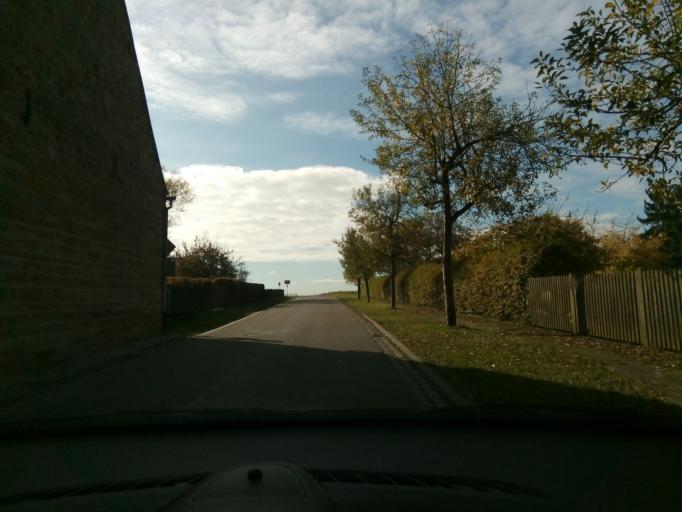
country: DE
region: Bavaria
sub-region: Regierungsbezirk Unterfranken
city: Oberschwarzach
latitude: 49.8734
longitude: 10.4026
